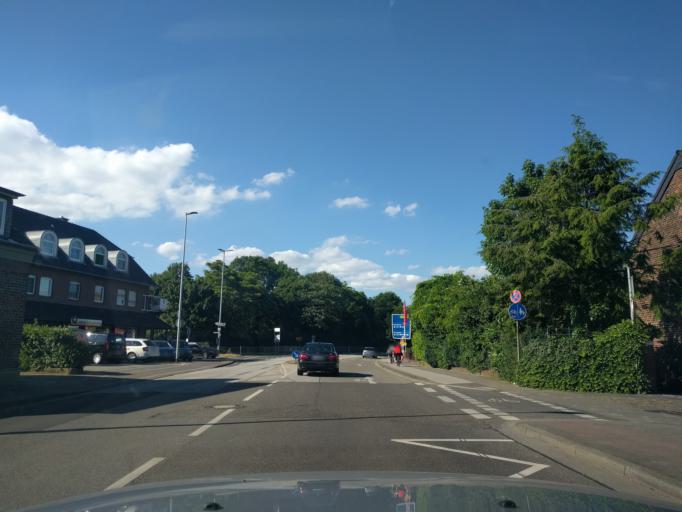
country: DE
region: North Rhine-Westphalia
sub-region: Regierungsbezirk Dusseldorf
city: Kaarst
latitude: 51.2343
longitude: 6.6160
